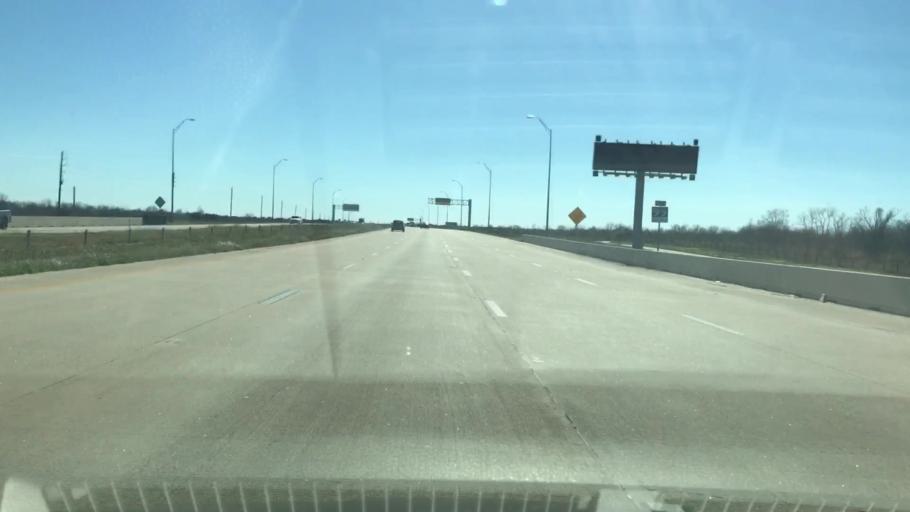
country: US
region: Texas
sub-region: Harris County
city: Cypress
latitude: 29.9889
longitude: -95.7695
